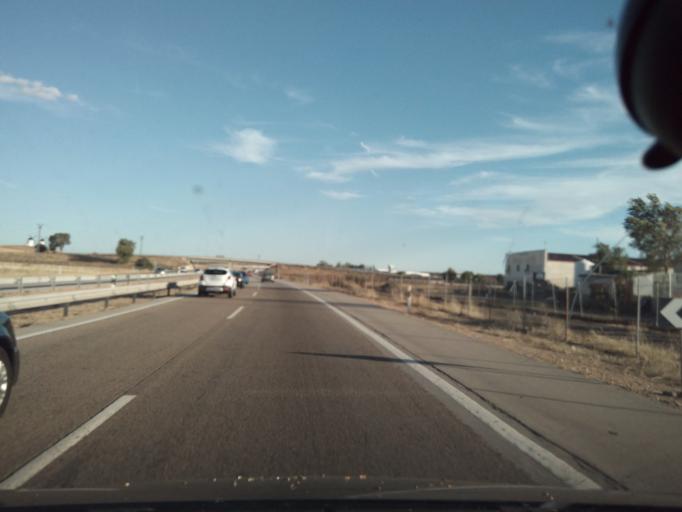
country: ES
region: Castille-La Mancha
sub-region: Province of Toledo
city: Tembleque
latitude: 39.6982
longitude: -3.4986
